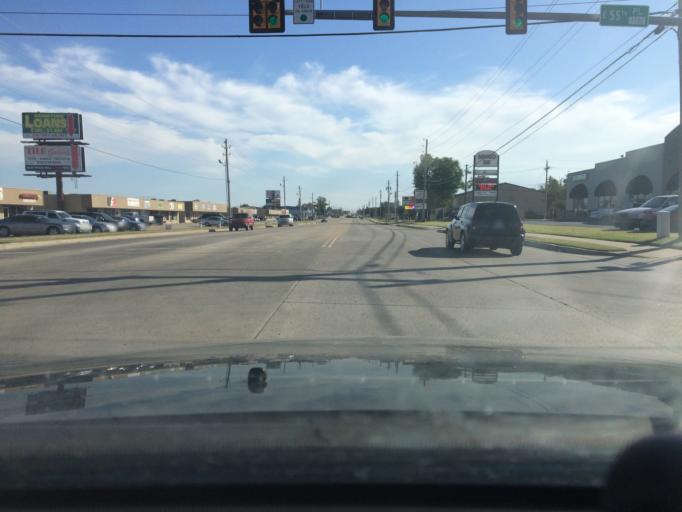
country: US
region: Oklahoma
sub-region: Tulsa County
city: Broken Arrow
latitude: 36.0837
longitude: -95.8686
